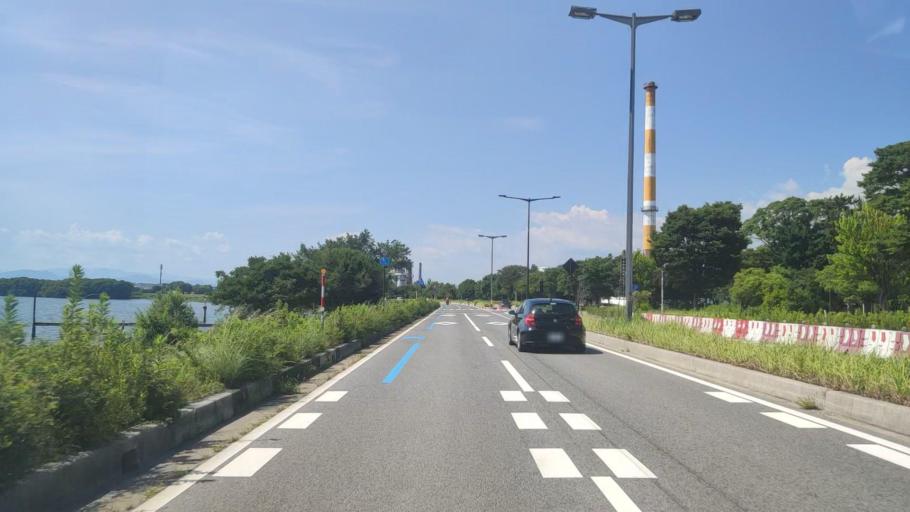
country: JP
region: Shiga Prefecture
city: Nagahama
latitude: 35.3788
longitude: 136.2578
